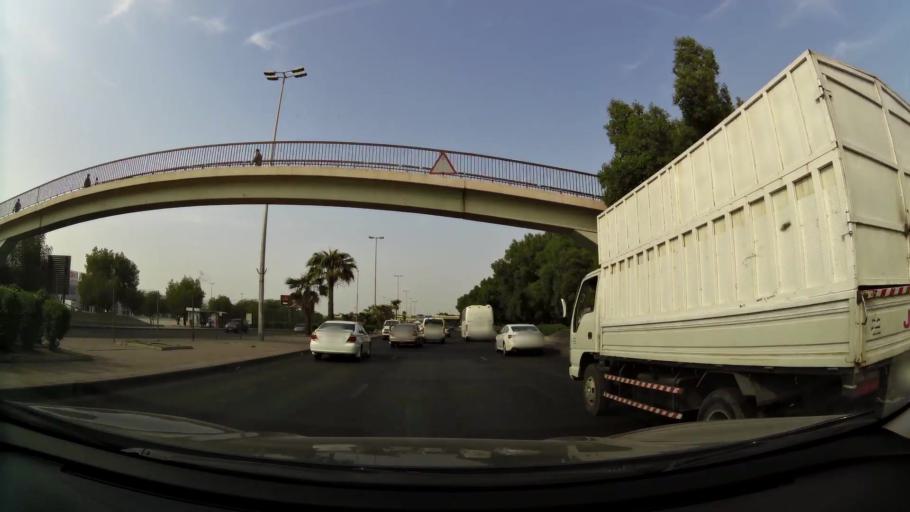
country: KW
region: Al Asimah
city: Ash Shamiyah
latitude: 29.3143
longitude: 47.9615
